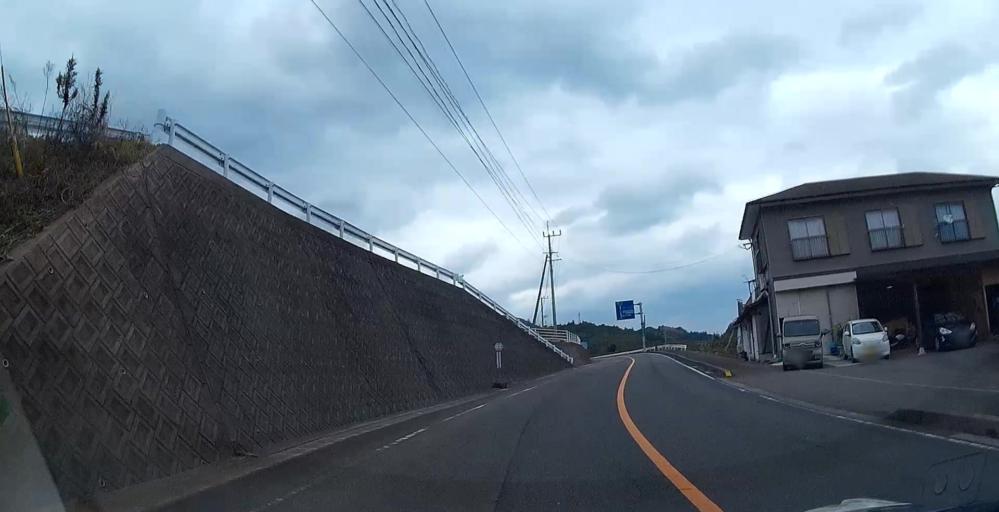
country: JP
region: Kagoshima
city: Akune
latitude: 32.1050
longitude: 130.1655
